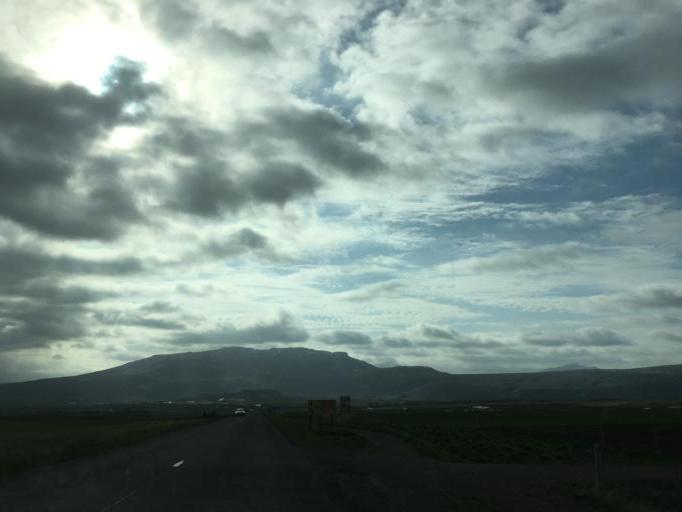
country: IS
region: South
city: Selfoss
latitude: 64.3092
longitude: -20.2257
